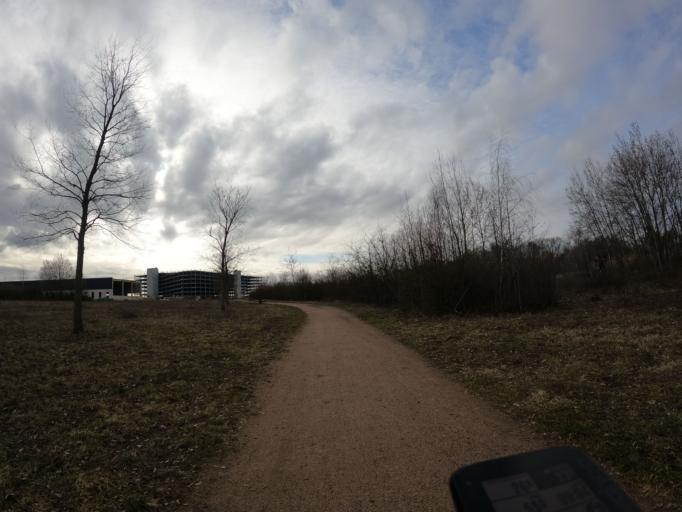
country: DE
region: Brandenburg
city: Schonefeld
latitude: 52.3915
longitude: 13.5335
